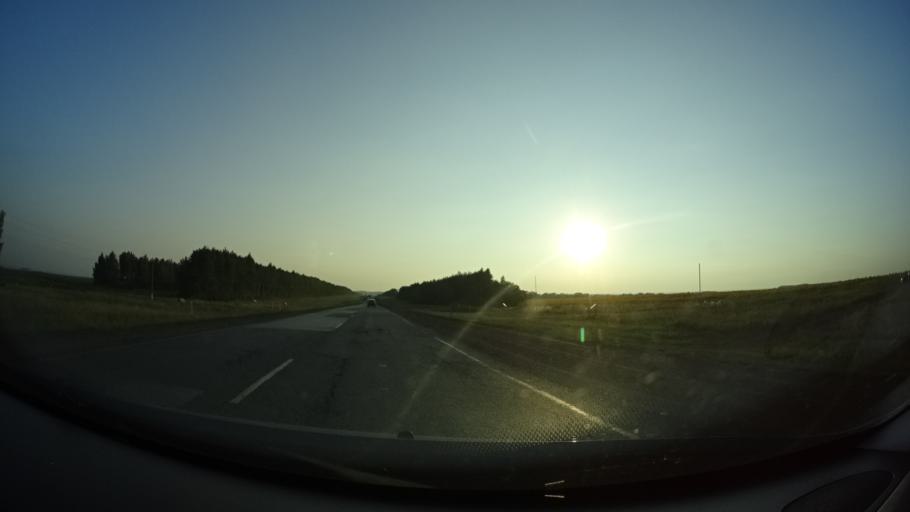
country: RU
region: Samara
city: Isakly
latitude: 54.0070
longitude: 51.6271
